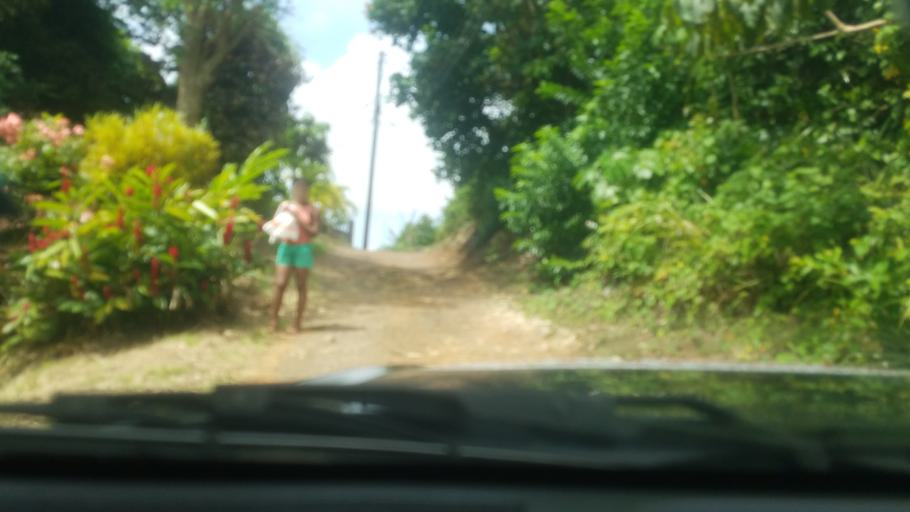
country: LC
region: Micoud Quarter
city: Micoud
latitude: 13.8059
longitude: -60.9492
